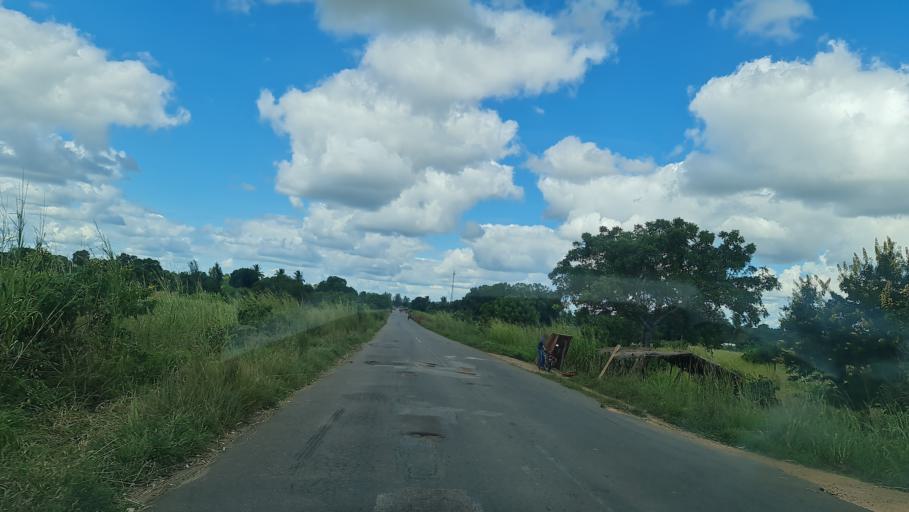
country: MZ
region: Zambezia
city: Quelimane
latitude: -17.5171
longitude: 36.2618
